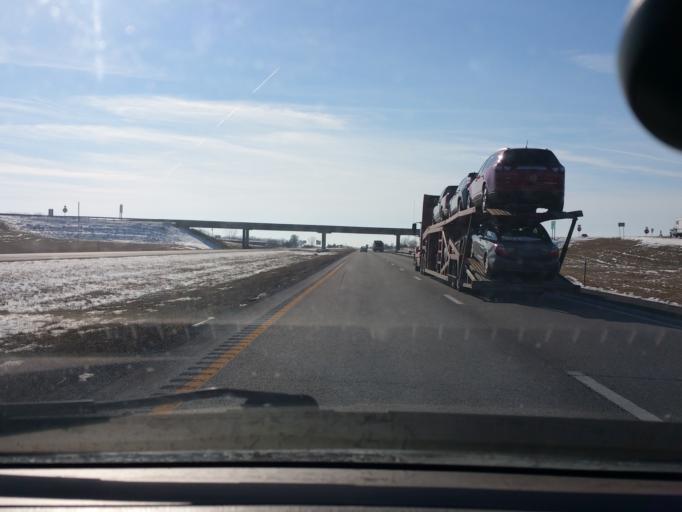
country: US
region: Missouri
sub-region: Clinton County
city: Cameron
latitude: 39.8553
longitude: -94.1762
